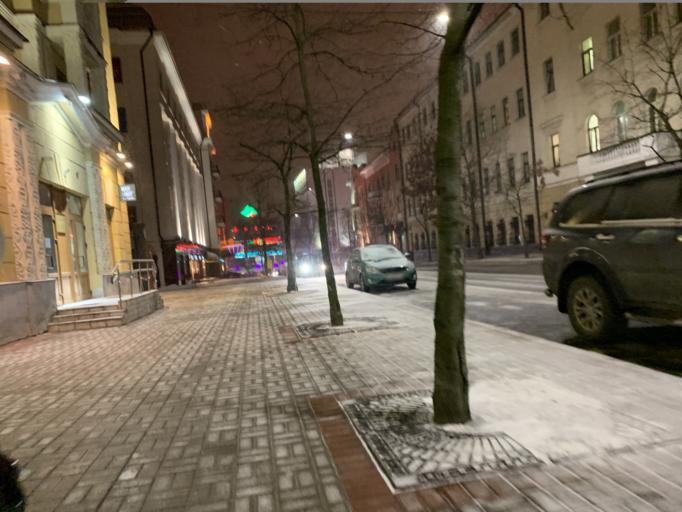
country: BY
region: Minsk
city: Minsk
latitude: 53.8956
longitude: 27.5536
